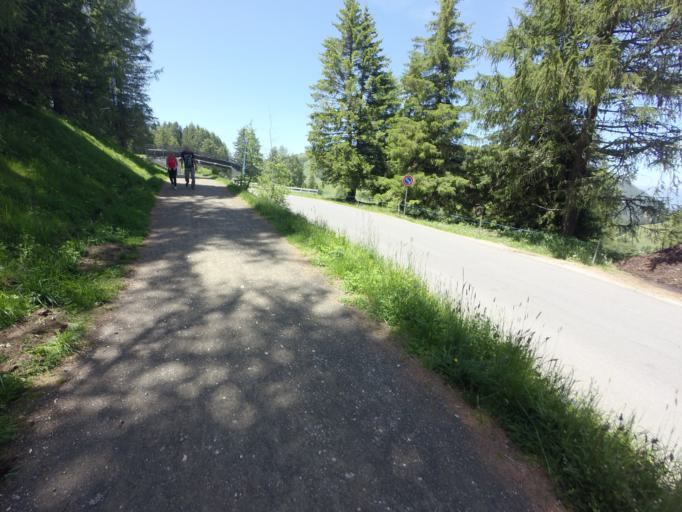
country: IT
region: Trentino-Alto Adige
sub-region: Bolzano
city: Ortisei
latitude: 46.5417
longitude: 11.6373
